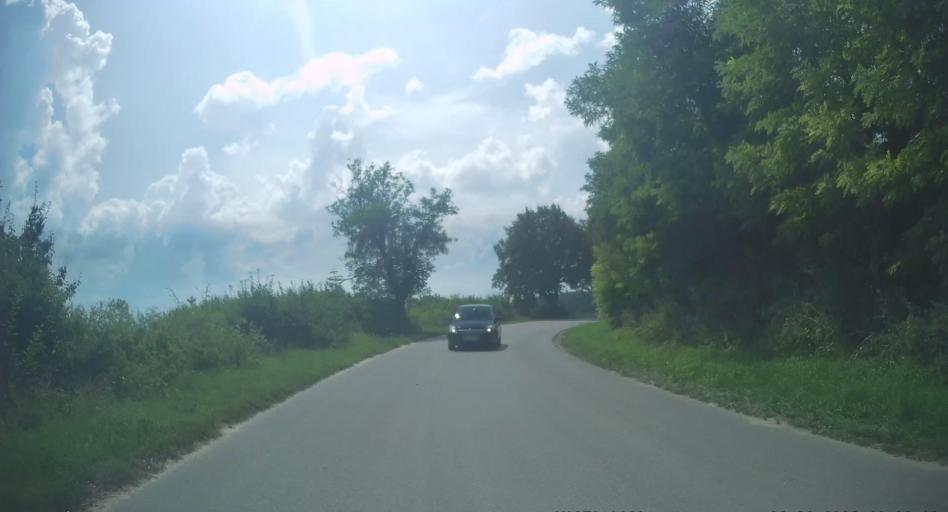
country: PL
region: Swietokrzyskie
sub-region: Powiat kielecki
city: Checiny
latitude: 50.7930
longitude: 20.4544
